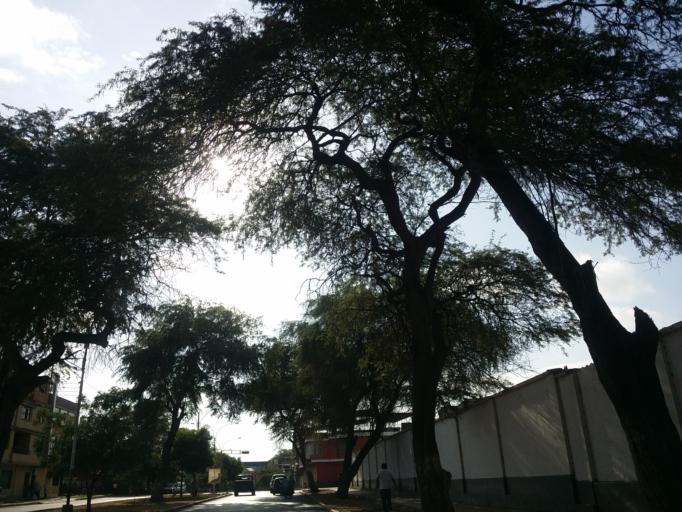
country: PE
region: Piura
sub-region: Provincia de Piura
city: Piura
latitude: -5.1839
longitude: -80.6274
